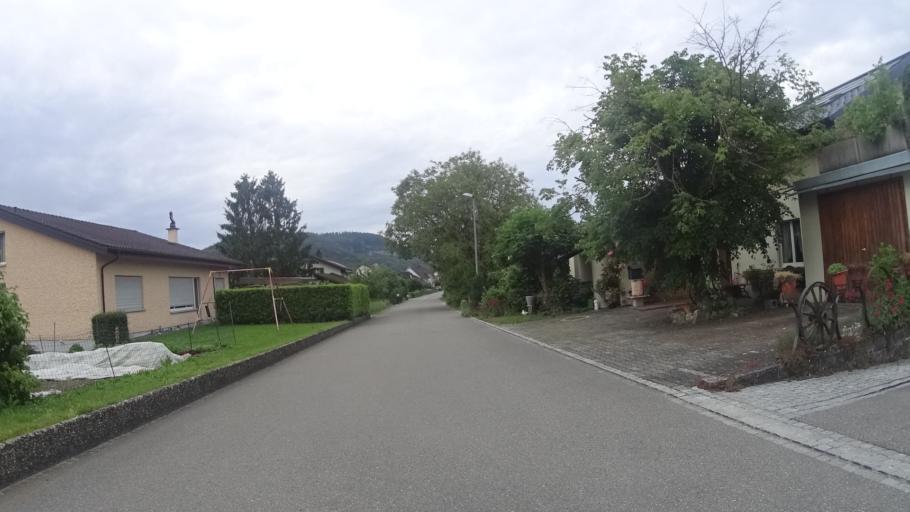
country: CH
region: Aargau
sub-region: Bezirk Baden
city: Wurenlingen
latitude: 47.5387
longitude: 8.2570
